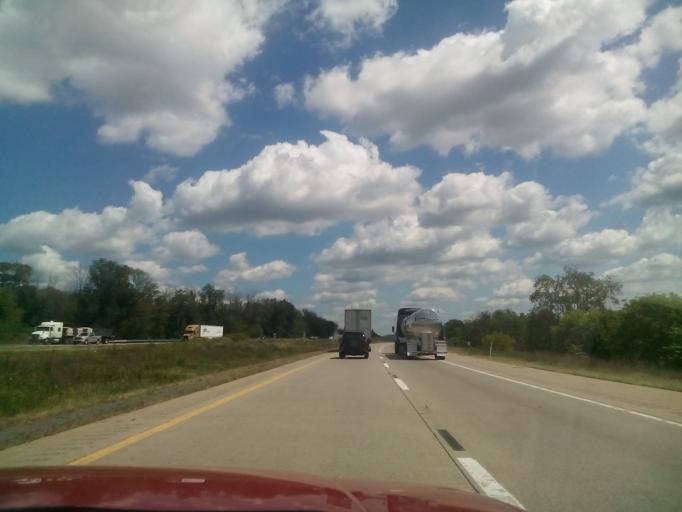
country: US
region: Pennsylvania
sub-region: Northumberland County
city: Riverside
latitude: 40.9897
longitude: -76.6795
